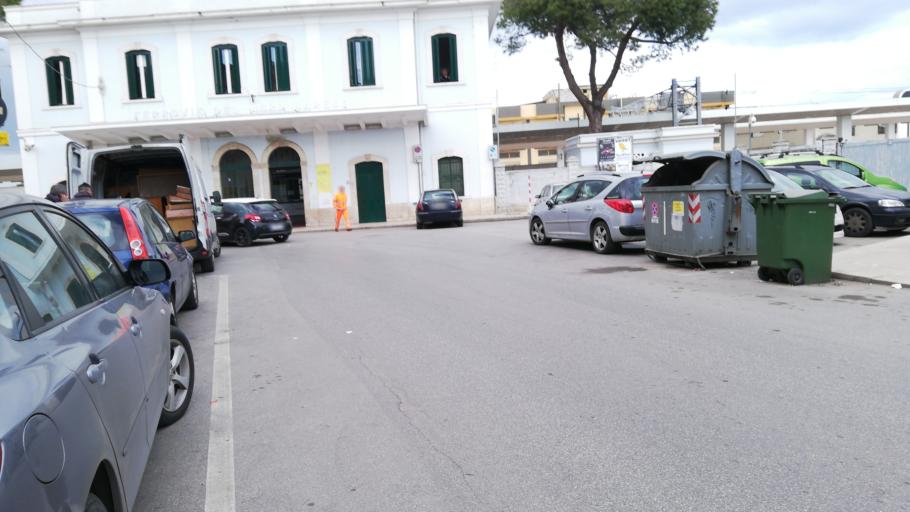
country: IT
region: Apulia
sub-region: Provincia di Bari
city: Bitonto
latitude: 41.1129
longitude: 16.6850
